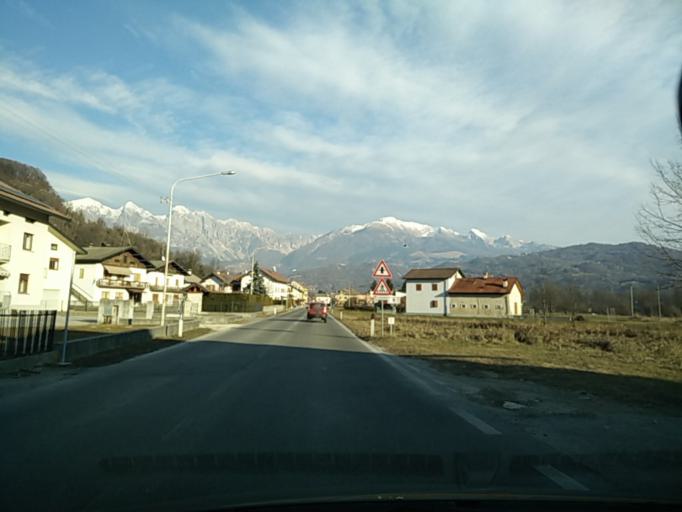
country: IT
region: Veneto
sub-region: Provincia di Belluno
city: Farra d'Alpago
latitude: 46.1320
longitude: 12.3334
